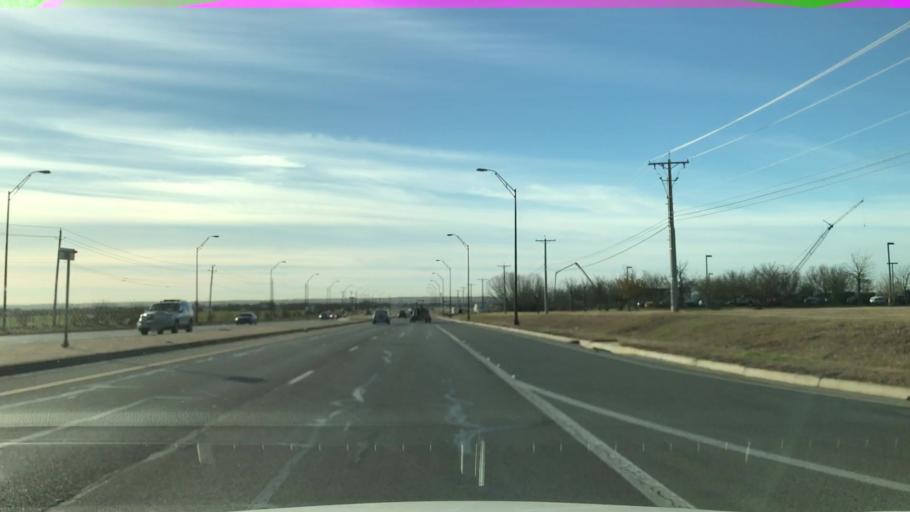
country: US
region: Texas
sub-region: Williamson County
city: Round Rock
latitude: 30.5671
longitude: -97.6486
